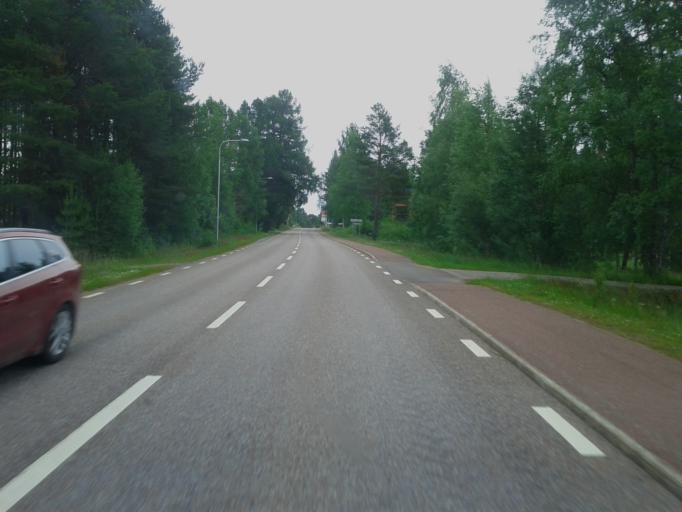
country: NO
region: Hedmark
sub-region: Trysil
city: Innbygda
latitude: 61.6947
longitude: 13.1203
